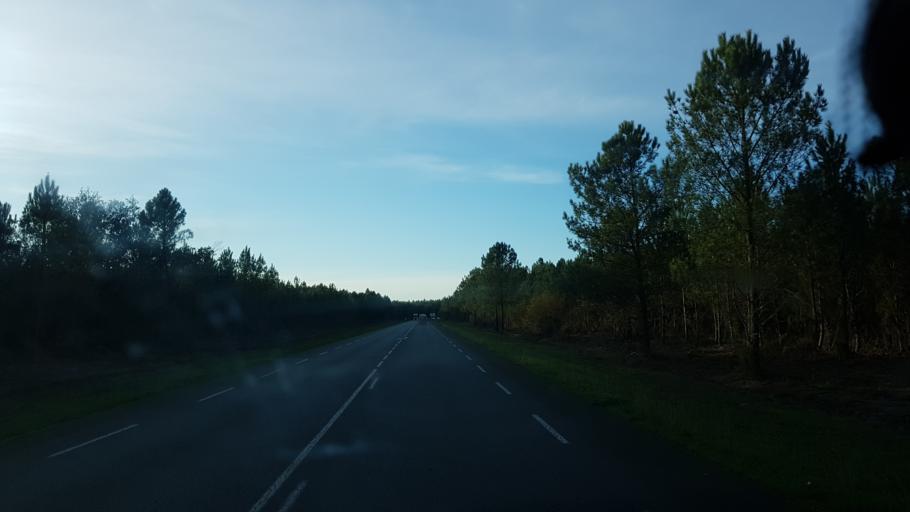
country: FR
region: Aquitaine
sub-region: Departement de la Gironde
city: Martignas-sur-Jalle
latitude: 44.8323
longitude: -0.7961
